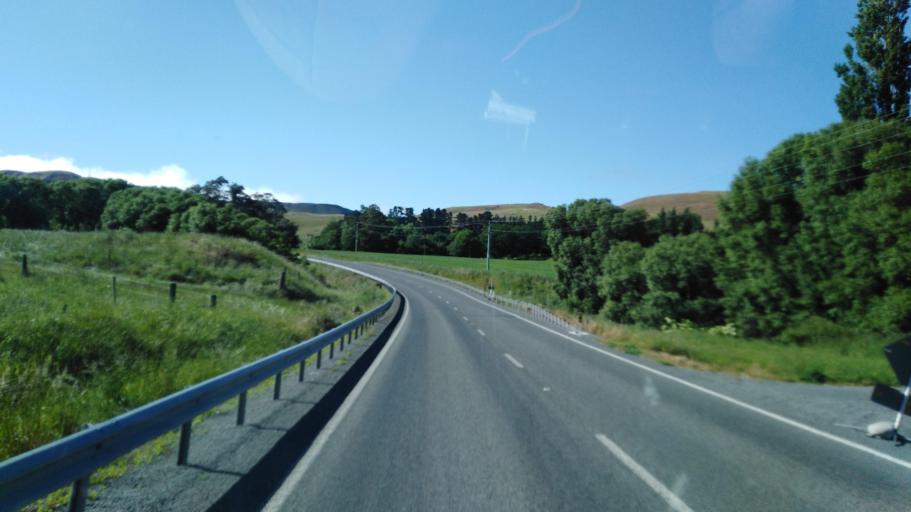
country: NZ
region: Canterbury
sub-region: Hurunui District
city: Amberley
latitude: -42.9763
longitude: 172.7074
